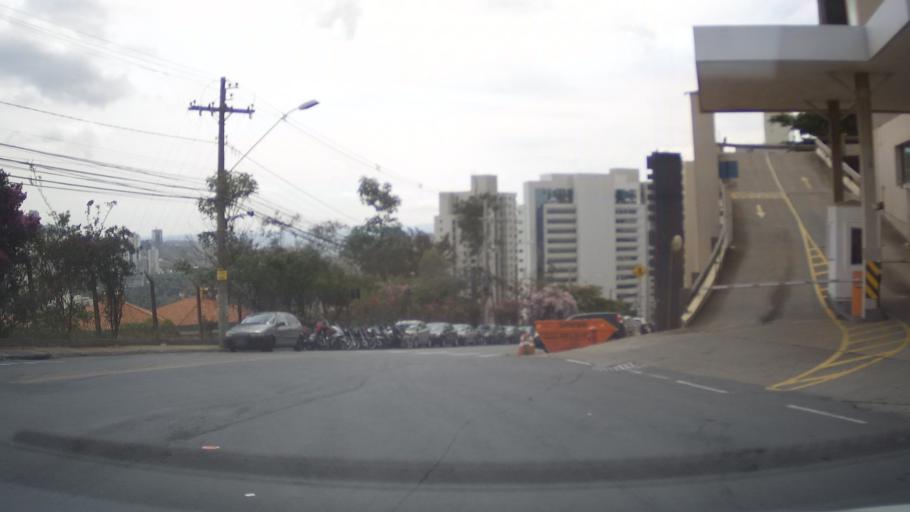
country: BR
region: Minas Gerais
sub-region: Belo Horizonte
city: Belo Horizonte
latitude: -19.9862
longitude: -43.9483
